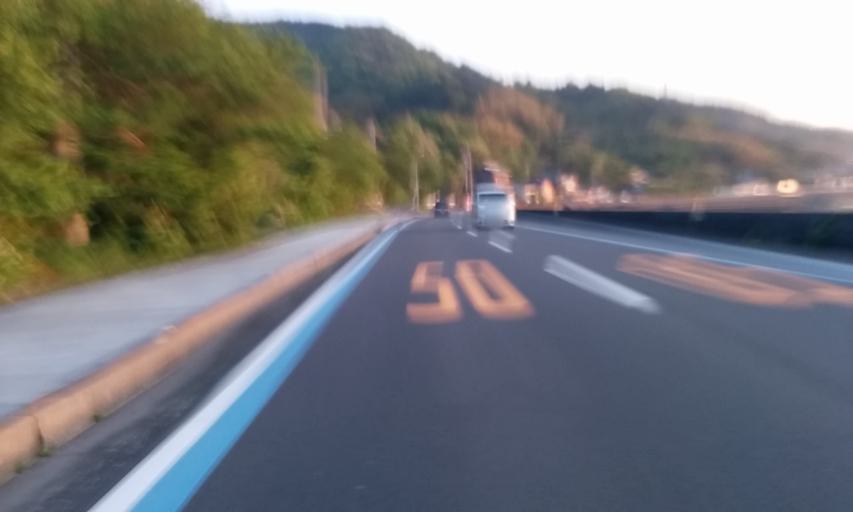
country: JP
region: Ehime
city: Iyo
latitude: 33.6814
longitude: 132.6290
